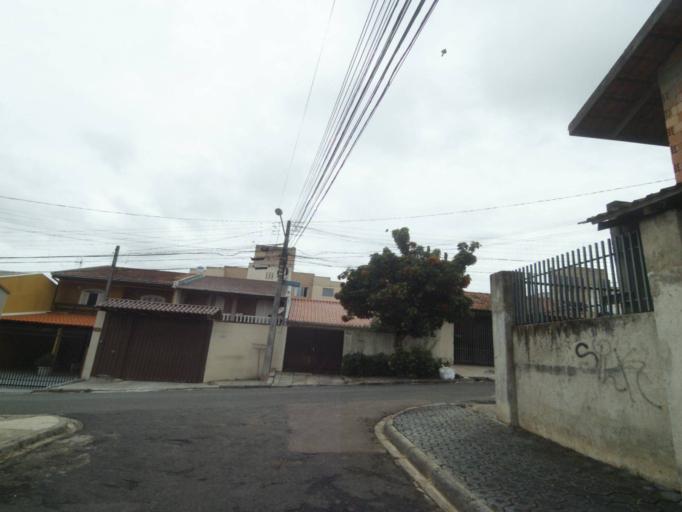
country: BR
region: Parana
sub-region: Curitiba
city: Curitiba
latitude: -25.4578
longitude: -49.3243
